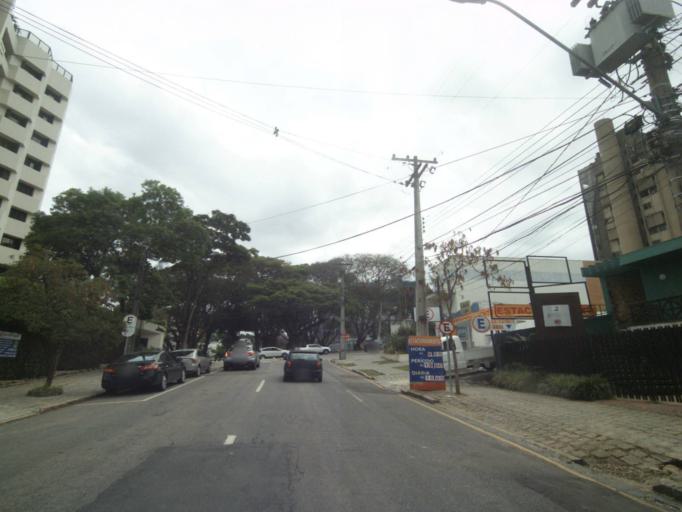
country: BR
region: Parana
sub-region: Curitiba
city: Curitiba
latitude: -25.4341
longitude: -49.2902
